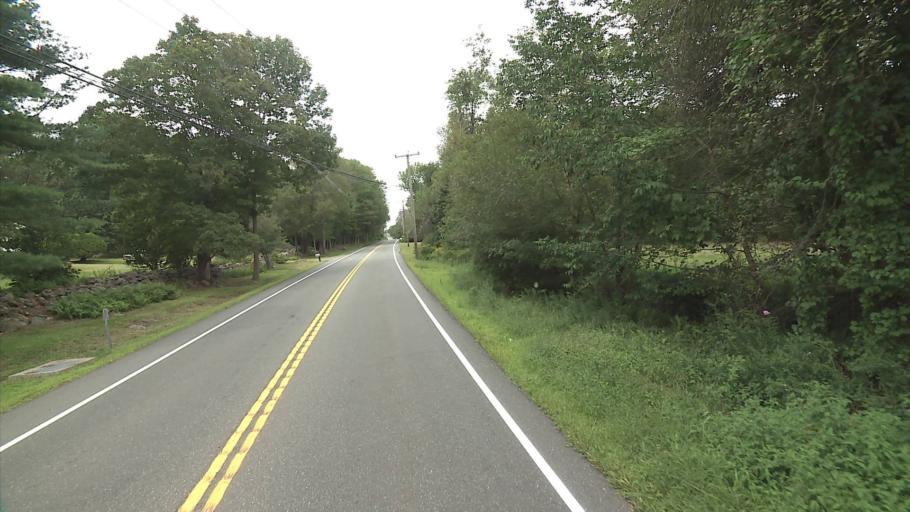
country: US
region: Connecticut
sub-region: New London County
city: Colchester
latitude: 41.5148
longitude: -72.2927
